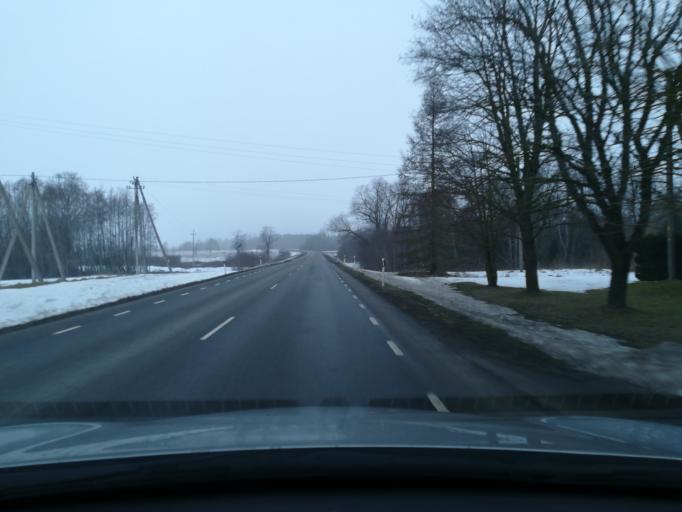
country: EE
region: Harju
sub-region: Raasiku vald
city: Raasiku
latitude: 59.3628
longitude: 25.1711
